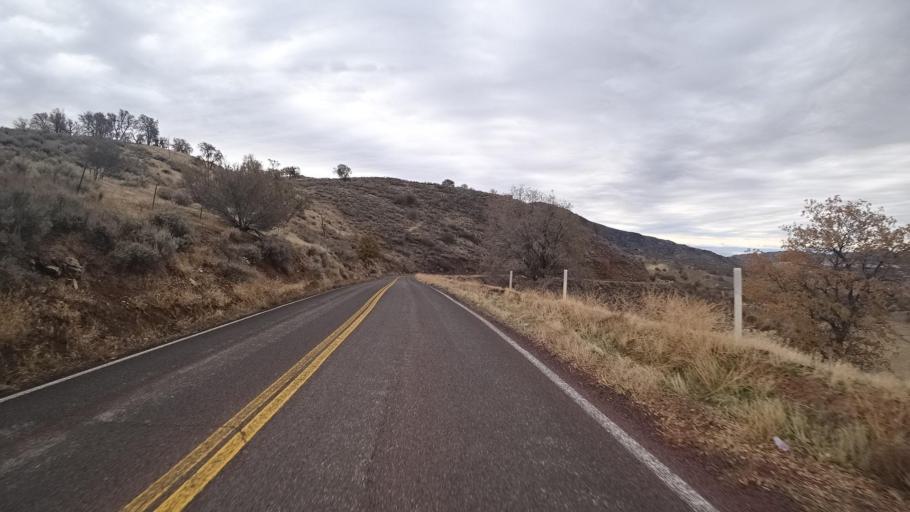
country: US
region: California
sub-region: Kern County
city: Golden Hills
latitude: 35.0945
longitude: -118.5526
